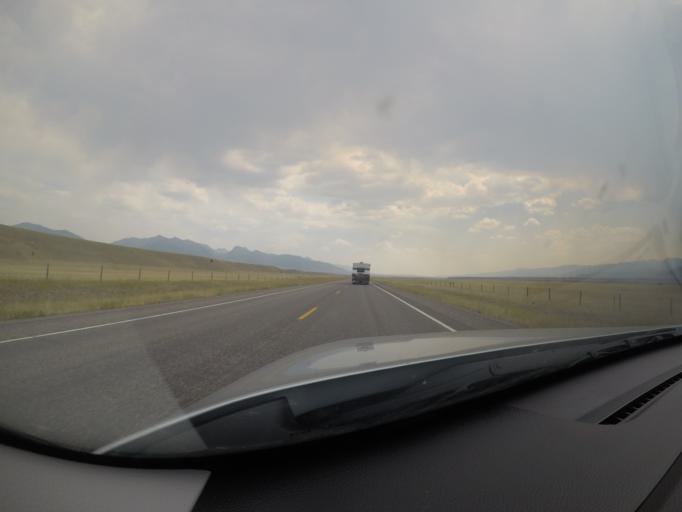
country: US
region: Montana
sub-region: Madison County
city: Virginia City
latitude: 45.1355
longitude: -111.6717
